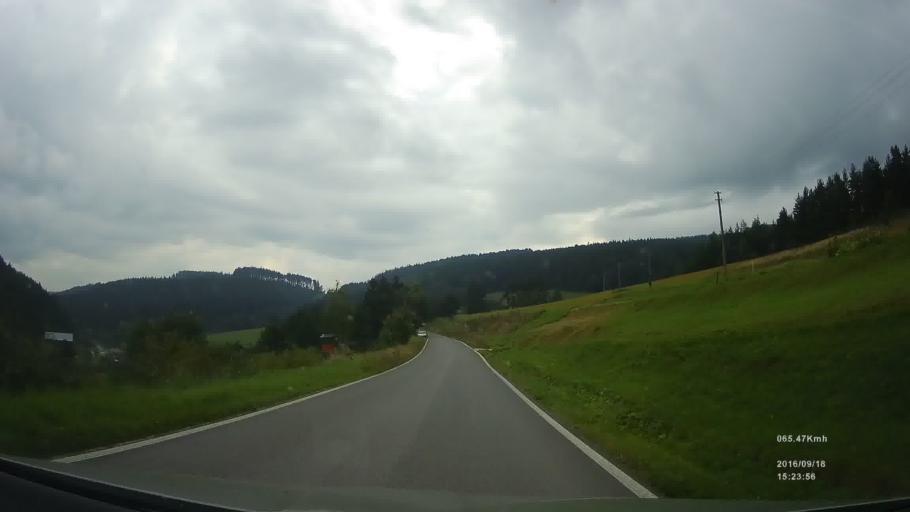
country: SK
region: Presovsky
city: Lubica
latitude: 49.0370
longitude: 20.4898
